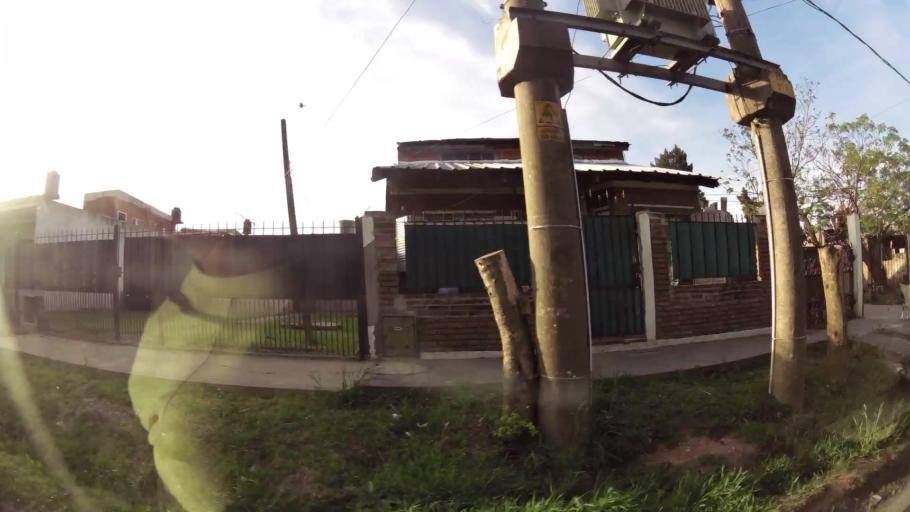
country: AR
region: Buenos Aires
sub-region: Partido de Almirante Brown
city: Adrogue
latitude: -34.7889
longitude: -58.3280
